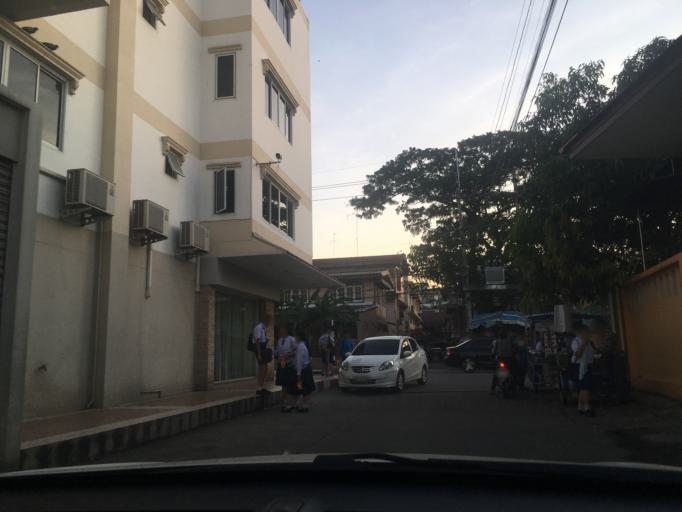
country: TH
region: Chon Buri
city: Ban Bueng
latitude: 13.3105
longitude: 101.1174
